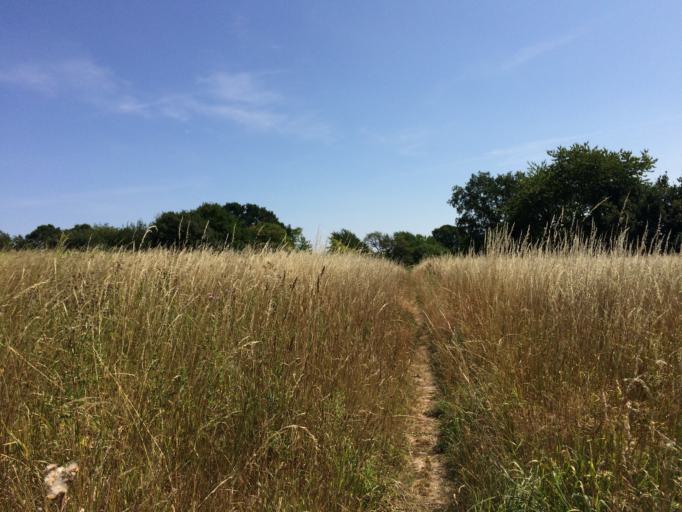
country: DK
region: Capital Region
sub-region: Fureso Kommune
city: Stavnsholt
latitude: 55.8306
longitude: 12.3987
